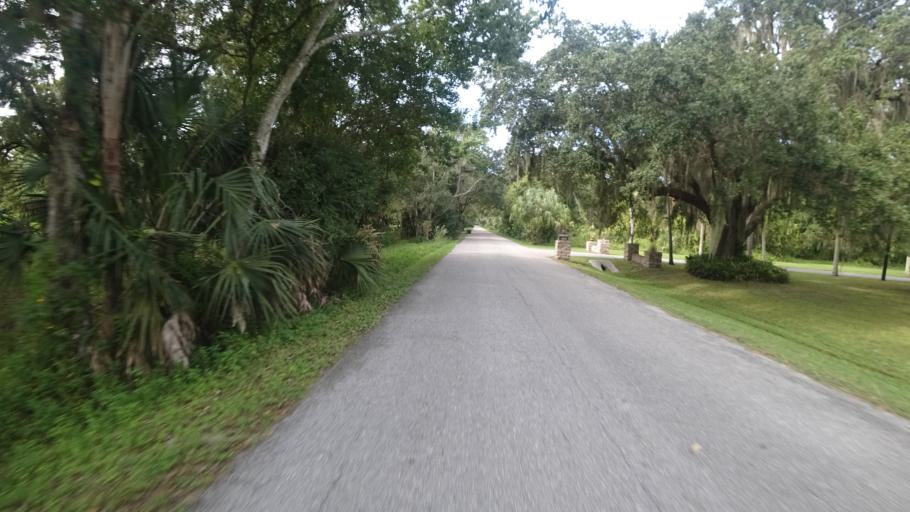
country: US
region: Florida
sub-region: Sarasota County
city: North Sarasota
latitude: 27.3870
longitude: -82.5250
